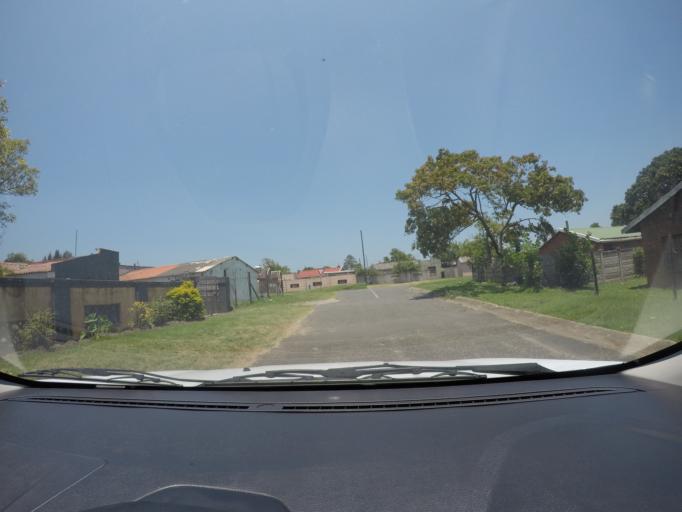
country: ZA
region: KwaZulu-Natal
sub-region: uThungulu District Municipality
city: eSikhawini
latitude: -28.8791
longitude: 31.9007
